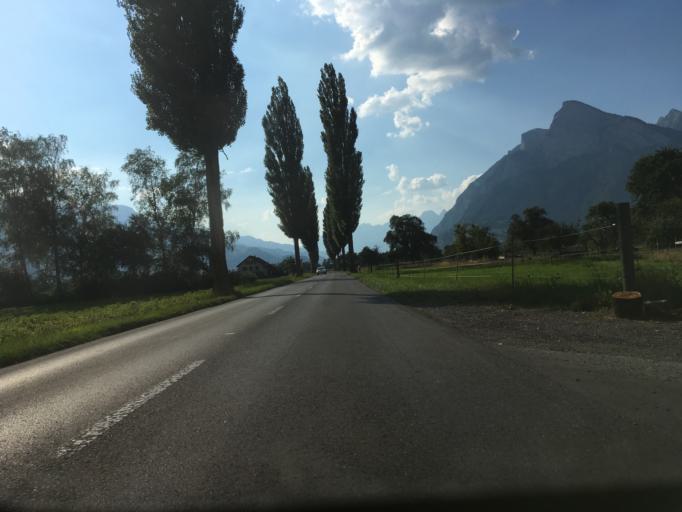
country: CH
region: Saint Gallen
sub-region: Wahlkreis Sarganserland
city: Bad Ragaz
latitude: 47.0244
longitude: 9.4755
